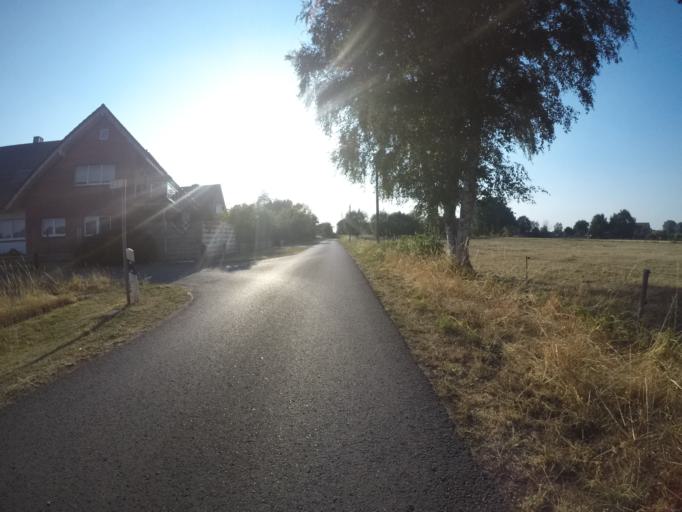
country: DE
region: North Rhine-Westphalia
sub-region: Regierungsbezirk Dusseldorf
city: Bocholt
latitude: 51.8499
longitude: 6.5752
